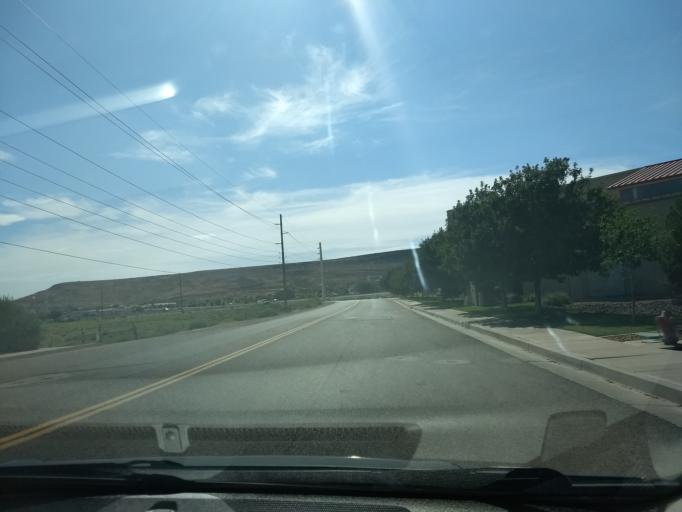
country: US
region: Utah
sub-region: Washington County
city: Saint George
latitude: 37.0871
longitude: -113.5776
